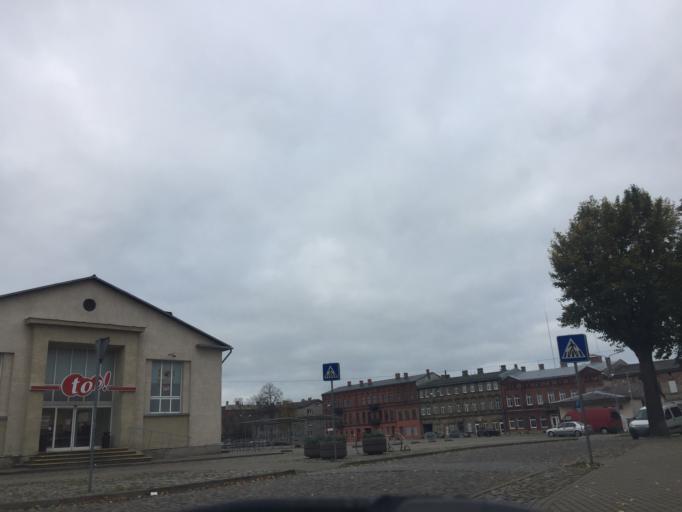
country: LV
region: Liepaja
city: Vec-Liepaja
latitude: 56.5524
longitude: 21.0704
